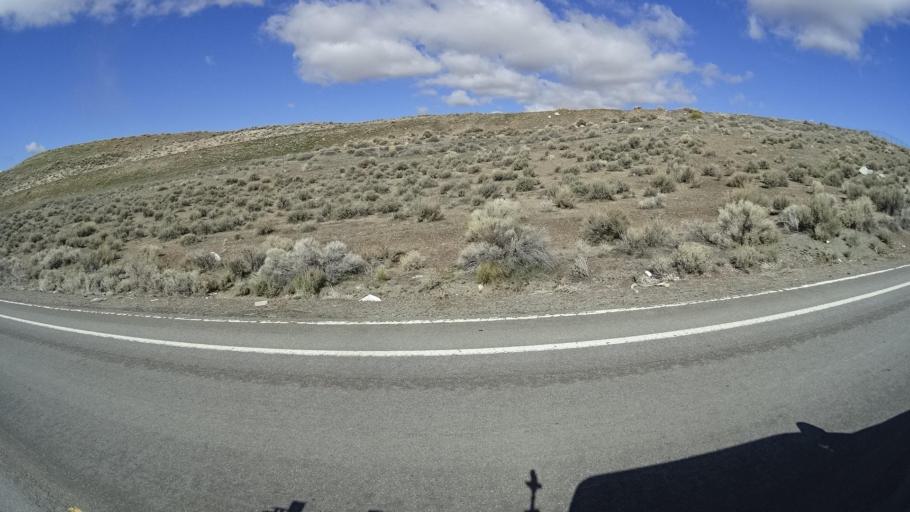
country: US
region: Nevada
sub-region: Washoe County
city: Lemmon Valley
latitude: 39.6627
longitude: -119.8610
